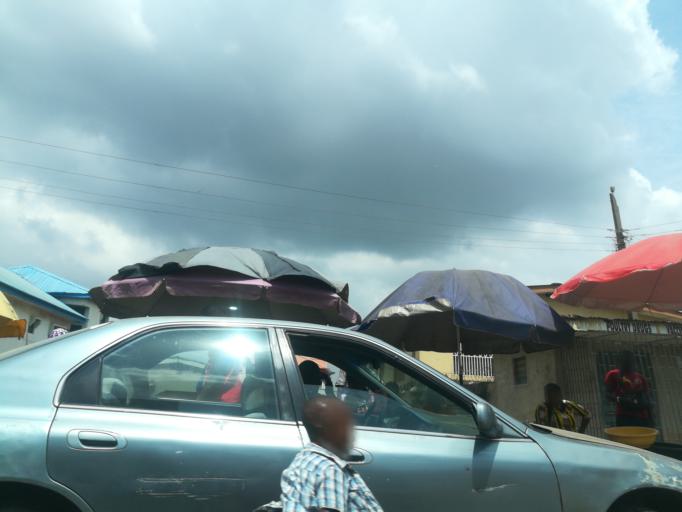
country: NG
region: Oyo
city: Ibadan
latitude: 7.4033
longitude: 3.9424
